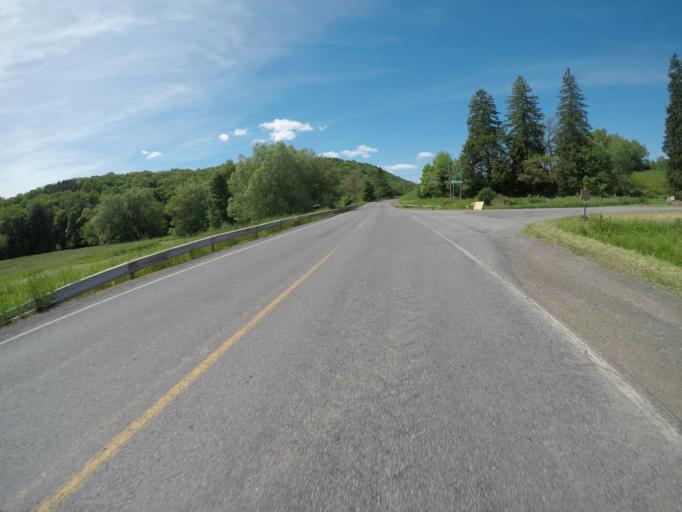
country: US
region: New York
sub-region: Delaware County
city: Delhi
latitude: 42.1699
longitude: -74.7891
